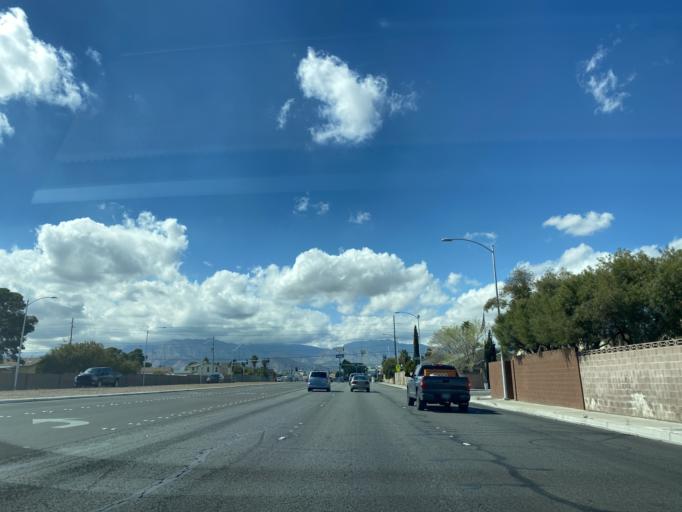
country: US
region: Nevada
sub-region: Clark County
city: Las Vegas
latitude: 36.2404
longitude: -115.2400
